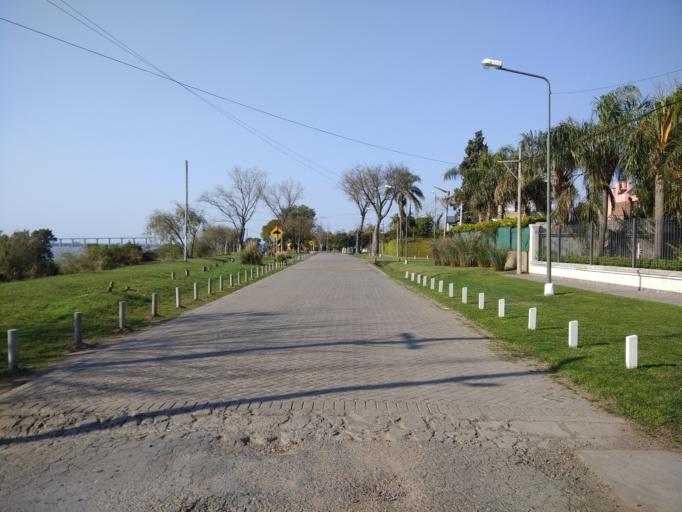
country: AR
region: Santa Fe
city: Granadero Baigorria
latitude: -32.8474
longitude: -60.6971
